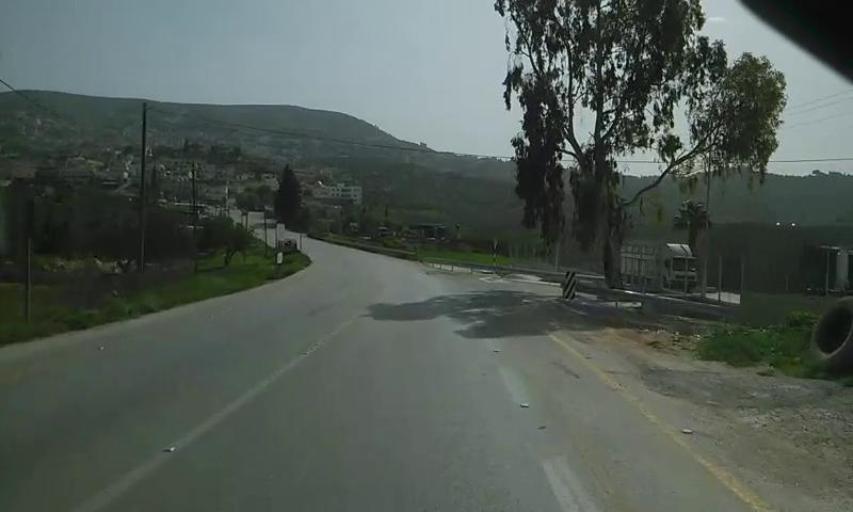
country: PS
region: West Bank
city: Al Fandaqumiyah
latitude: 32.3341
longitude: 35.2049
